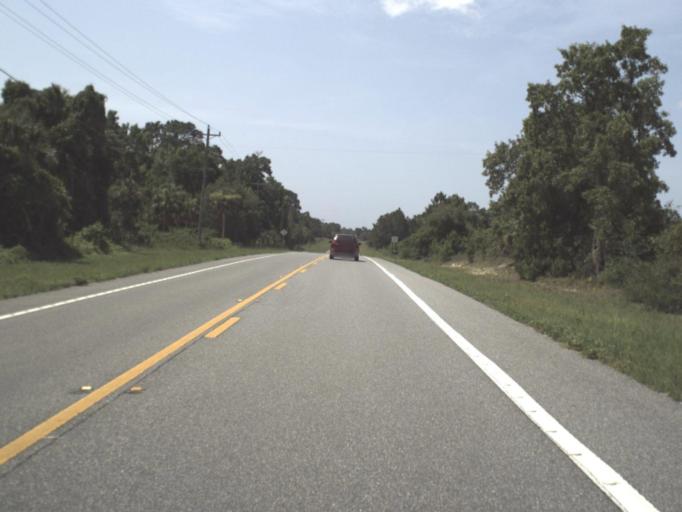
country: US
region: Florida
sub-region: Taylor County
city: Steinhatchee
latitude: 29.7072
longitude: -83.3584
